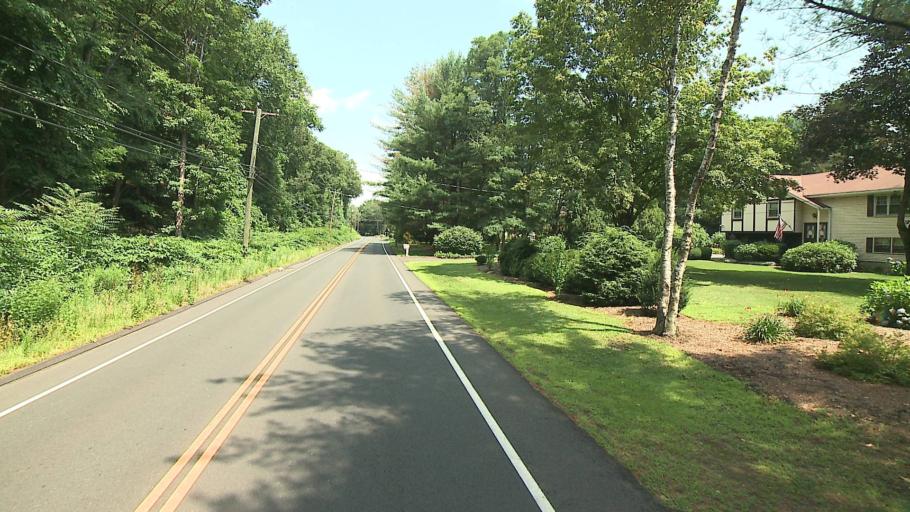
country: US
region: Connecticut
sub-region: Hartford County
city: Canton Valley
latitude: 41.8103
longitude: -72.8873
